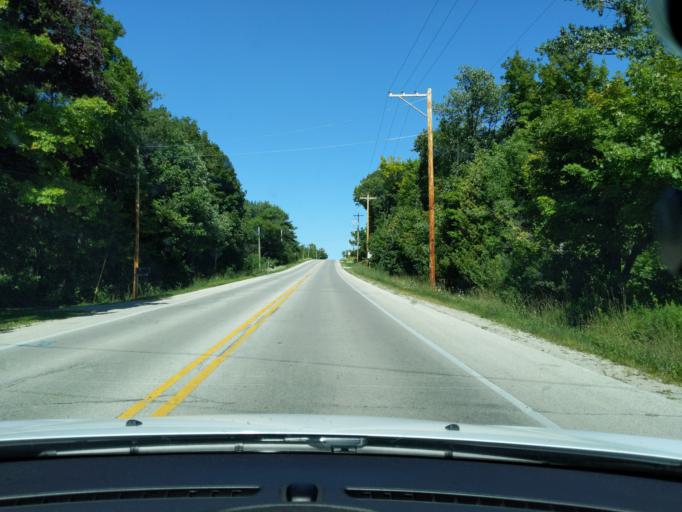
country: US
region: Wisconsin
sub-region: Door County
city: Sturgeon Bay
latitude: 45.2100
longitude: -87.1157
